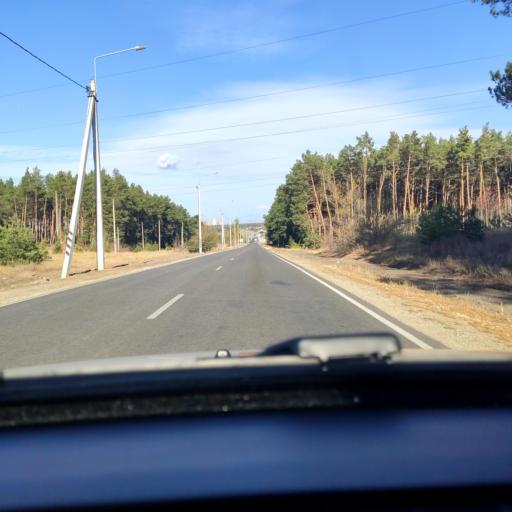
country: RU
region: Voronezj
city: Shilovo
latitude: 51.5329
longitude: 39.1402
